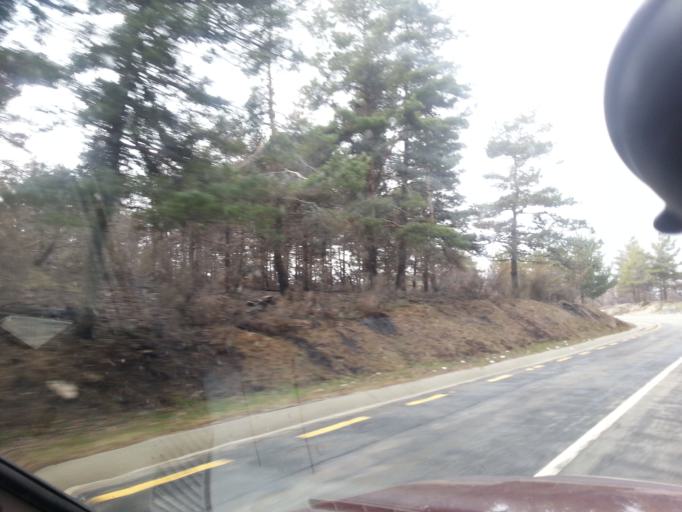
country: PT
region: Guarda
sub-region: Manteigas
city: Manteigas
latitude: 40.4120
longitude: -7.5762
